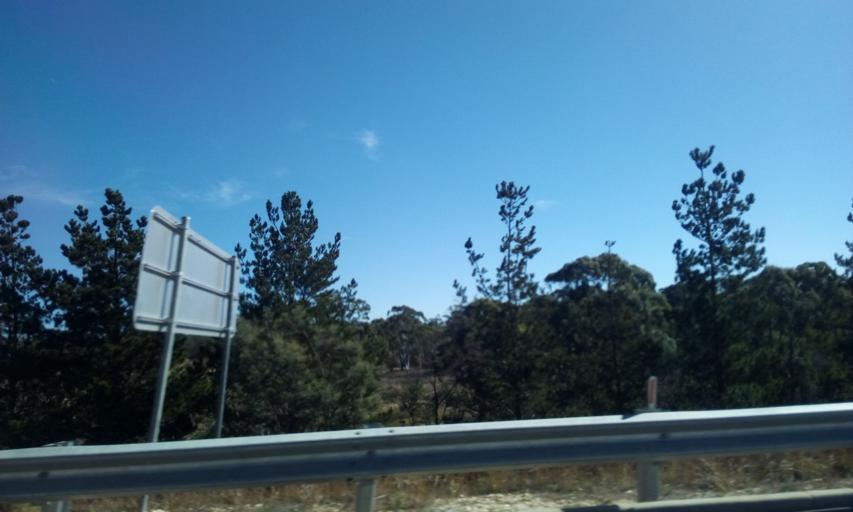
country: AU
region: New South Wales
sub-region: Yass Valley
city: Gundaroo
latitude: -35.1035
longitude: 149.3729
